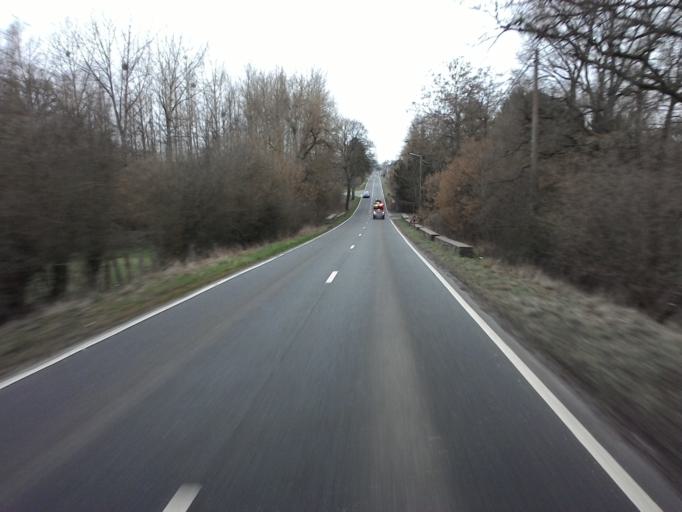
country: BE
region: Wallonia
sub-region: Province de Namur
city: Beauraing
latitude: 50.0958
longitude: 5.0211
